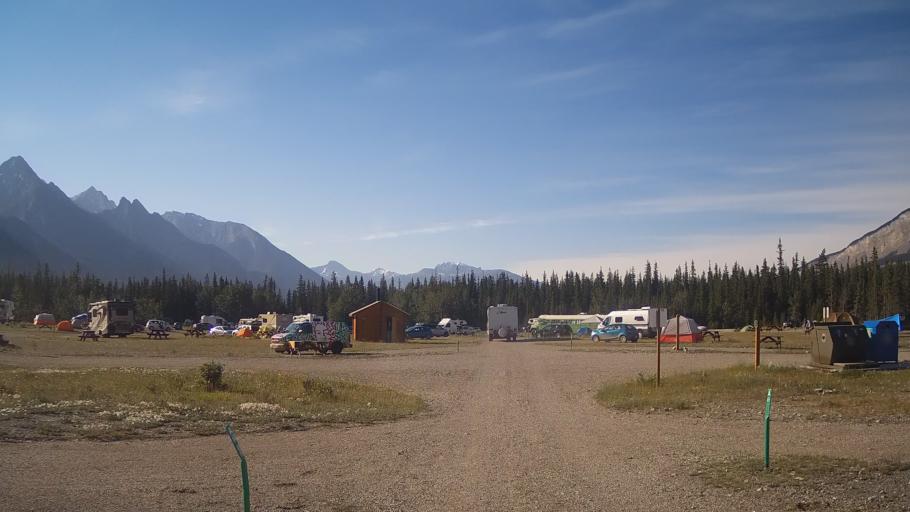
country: CA
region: Alberta
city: Jasper Park Lodge
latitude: 53.0170
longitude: -118.0855
